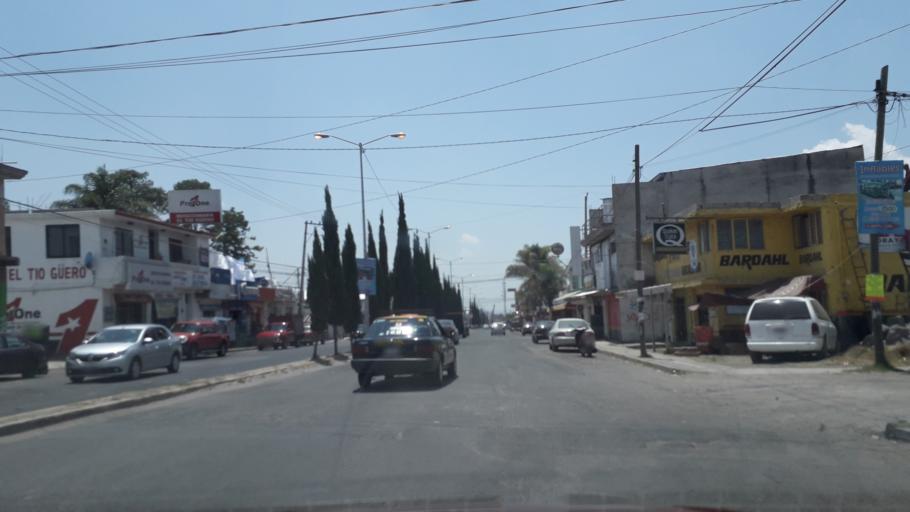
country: MX
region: Puebla
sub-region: Puebla
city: Primero de Mayo
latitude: 19.0723
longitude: -98.1149
